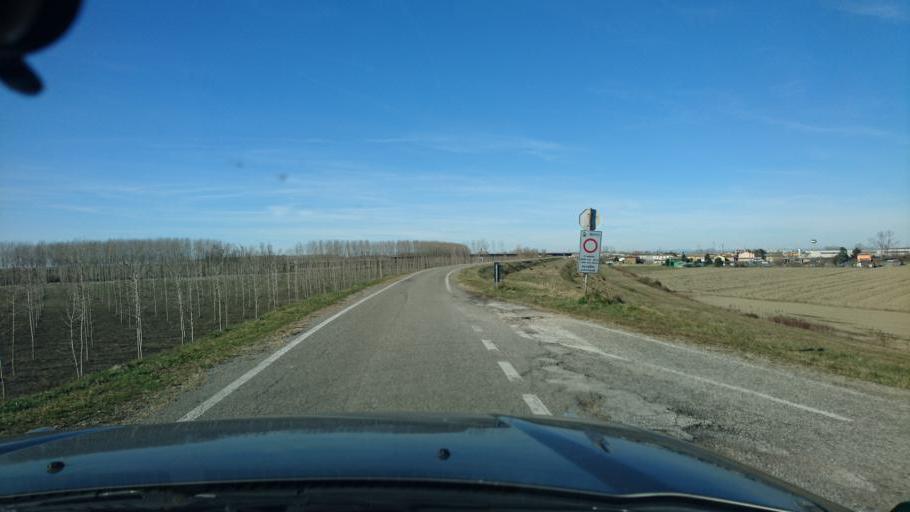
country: IT
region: Veneto
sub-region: Provincia di Rovigo
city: Ariano
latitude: 44.9347
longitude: 12.1312
